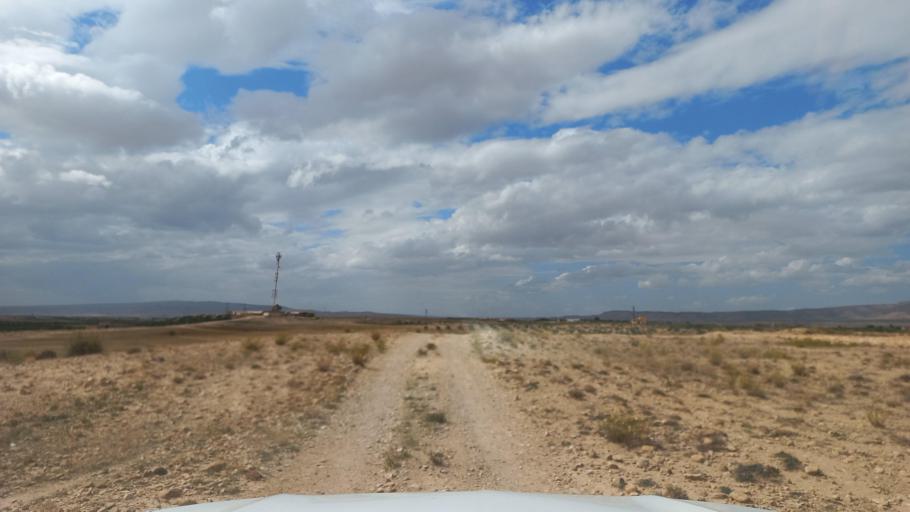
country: TN
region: Al Qasrayn
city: Sbiba
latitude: 35.3790
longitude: 9.1014
